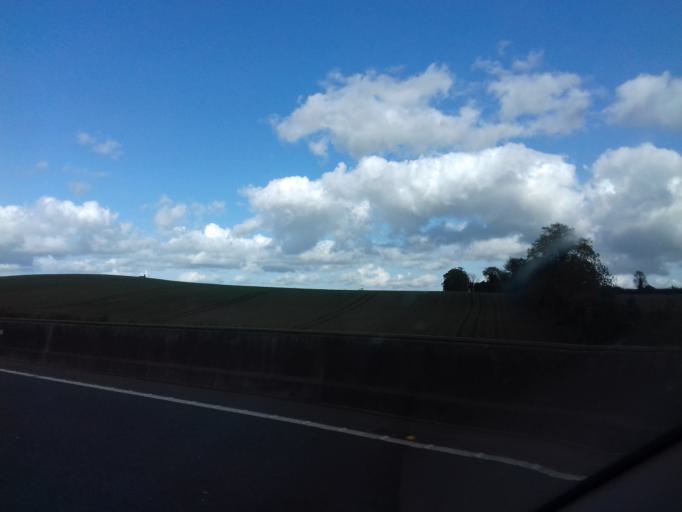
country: IE
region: Leinster
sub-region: Kilkenny
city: Kilkenny
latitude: 52.5645
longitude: -7.2392
